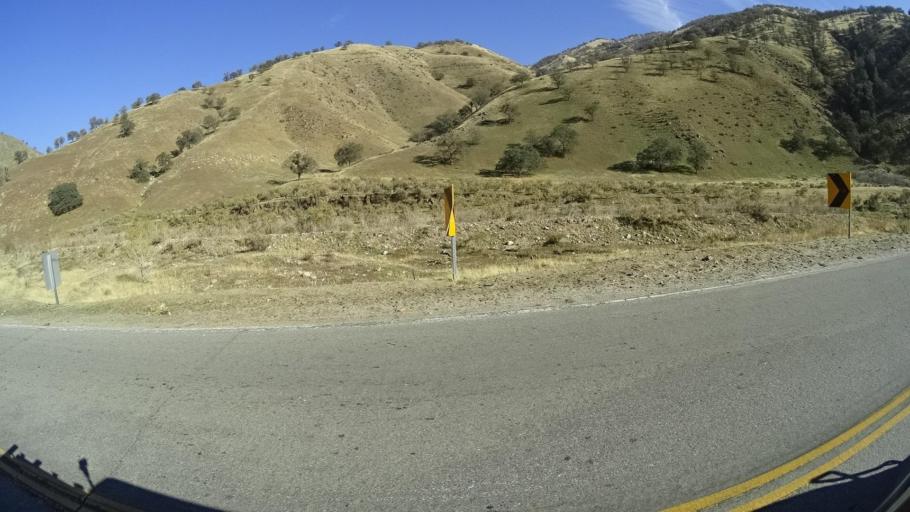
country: US
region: California
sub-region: Kern County
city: Bear Valley Springs
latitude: 35.2996
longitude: -118.5911
